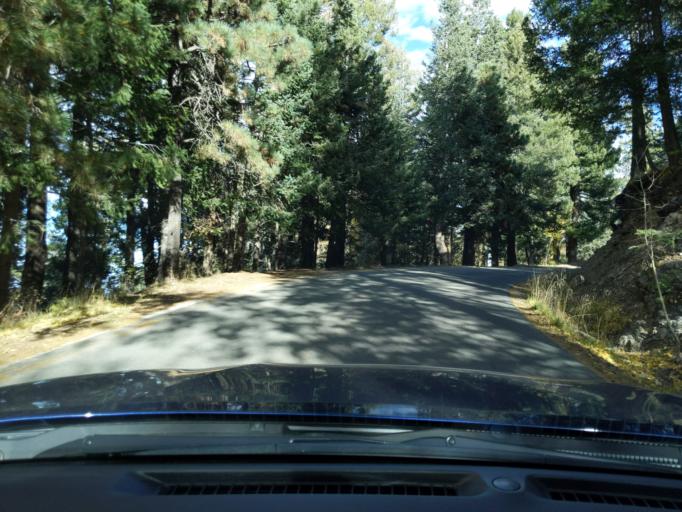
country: US
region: Arizona
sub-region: Pima County
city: Catalina
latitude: 32.4415
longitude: -110.7847
